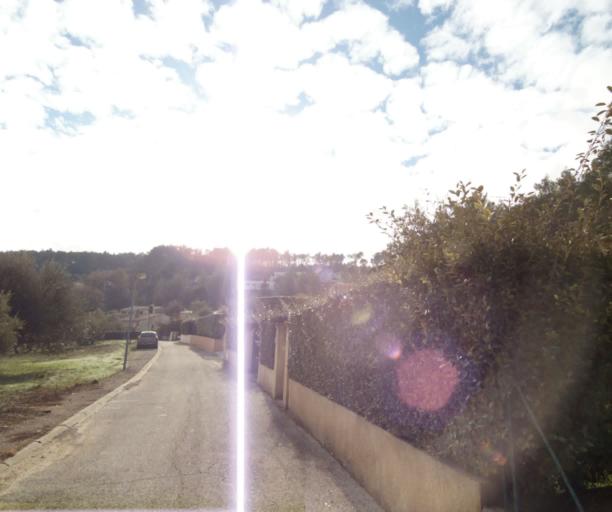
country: FR
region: Provence-Alpes-Cote d'Azur
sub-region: Departement du Var
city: Trans-en-Provence
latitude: 43.5003
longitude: 6.4812
